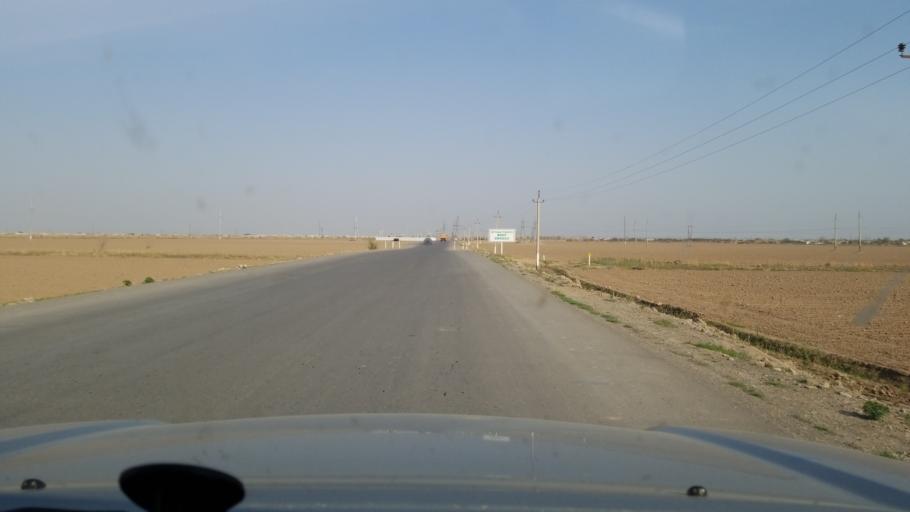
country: AF
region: Jowzjan
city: Khamyab
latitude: 37.6064
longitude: 65.7350
